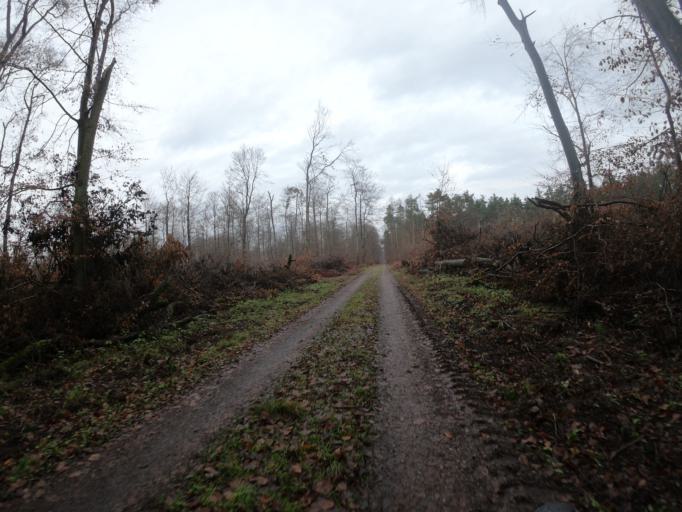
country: DE
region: Hesse
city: Morfelden-Walldorf
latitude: 49.9774
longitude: 8.6091
